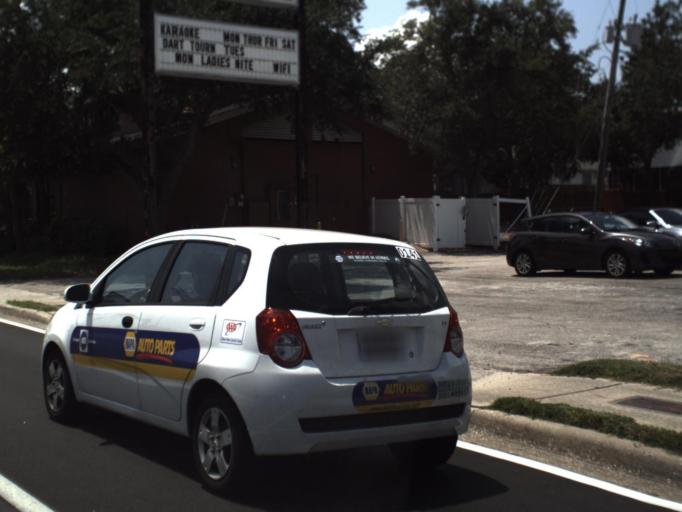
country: US
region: Florida
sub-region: Pinellas County
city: Lealman
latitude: 27.8001
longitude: -82.6386
